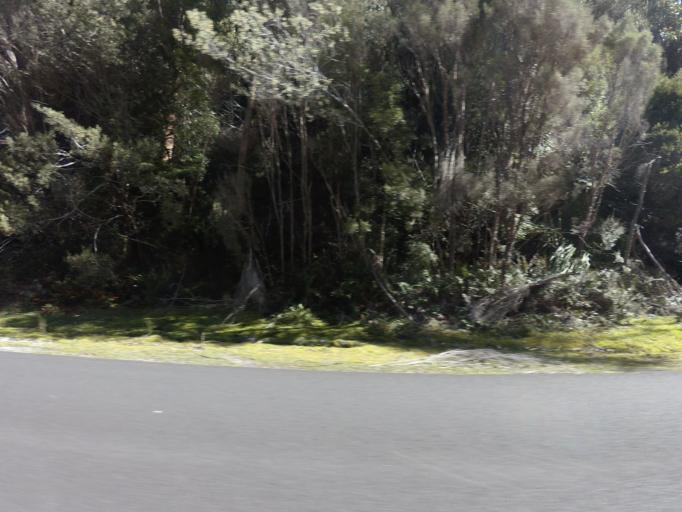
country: AU
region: Tasmania
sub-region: Derwent Valley
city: New Norfolk
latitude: -42.7326
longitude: 146.4754
